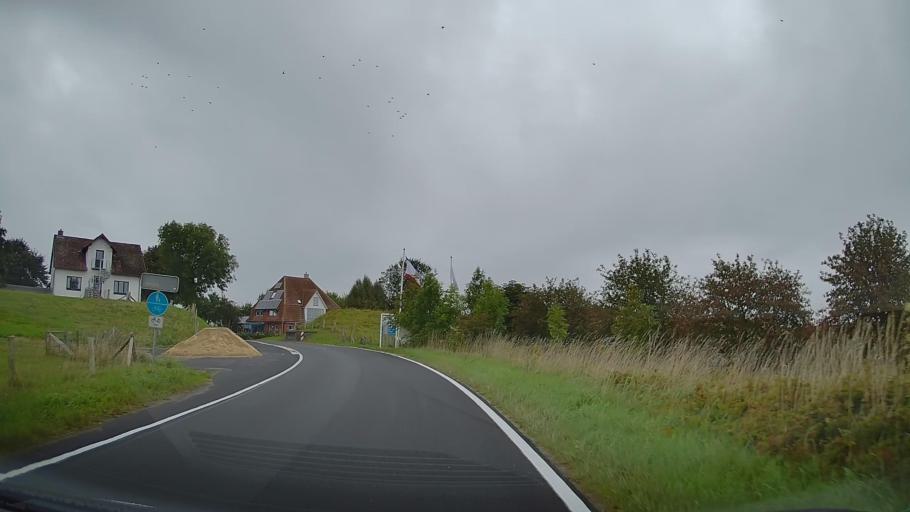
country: DE
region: Schleswig-Holstein
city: Friedrichsgabekoog
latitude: 54.1409
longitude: 8.9299
